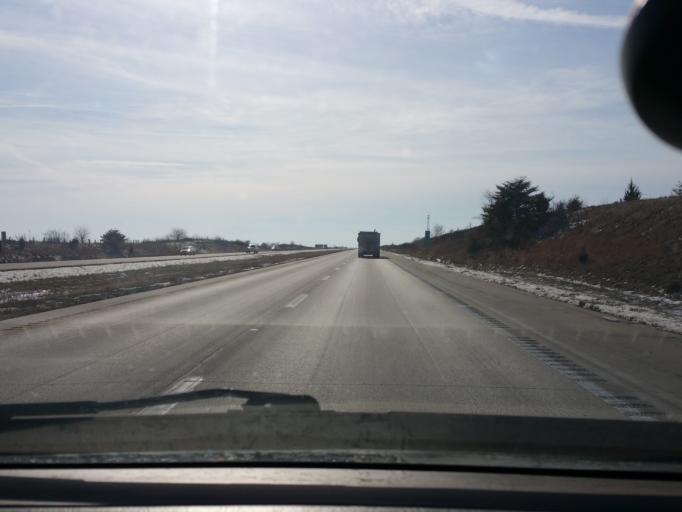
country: US
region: Missouri
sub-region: Clinton County
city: Lathrop
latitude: 39.5859
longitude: -94.2579
